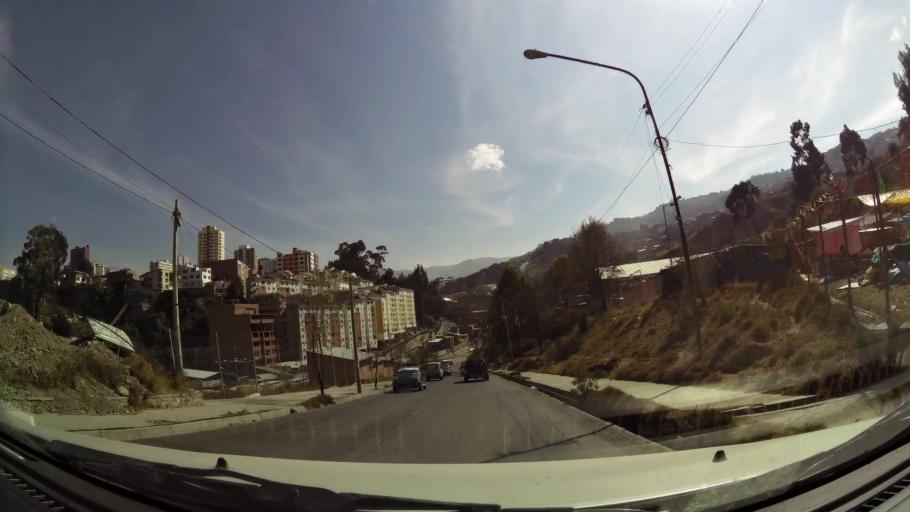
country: BO
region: La Paz
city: La Paz
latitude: -16.5068
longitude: -68.1155
